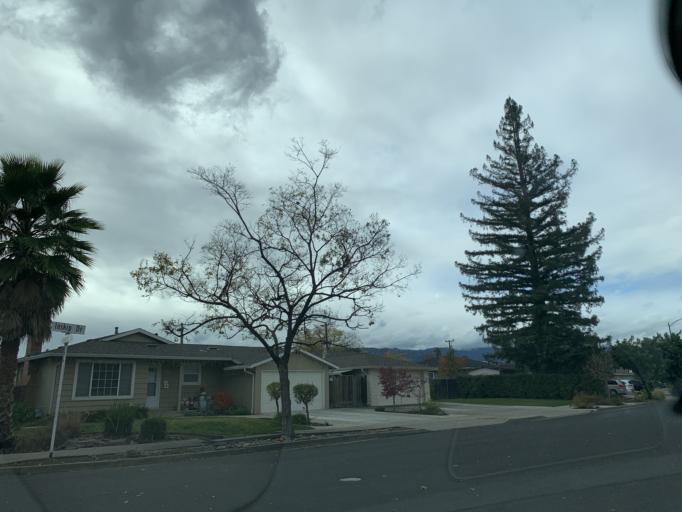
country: US
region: California
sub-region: Santa Clara County
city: Campbell
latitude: 37.2753
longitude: -121.9747
